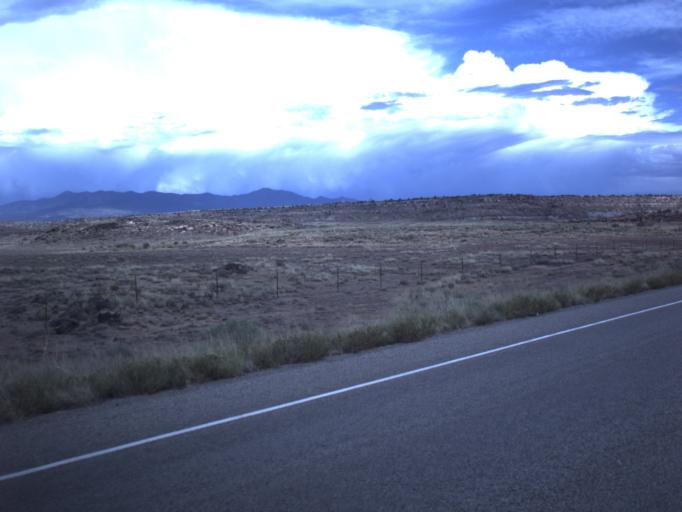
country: US
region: Colorado
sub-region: Montezuma County
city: Towaoc
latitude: 37.1691
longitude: -109.0855
